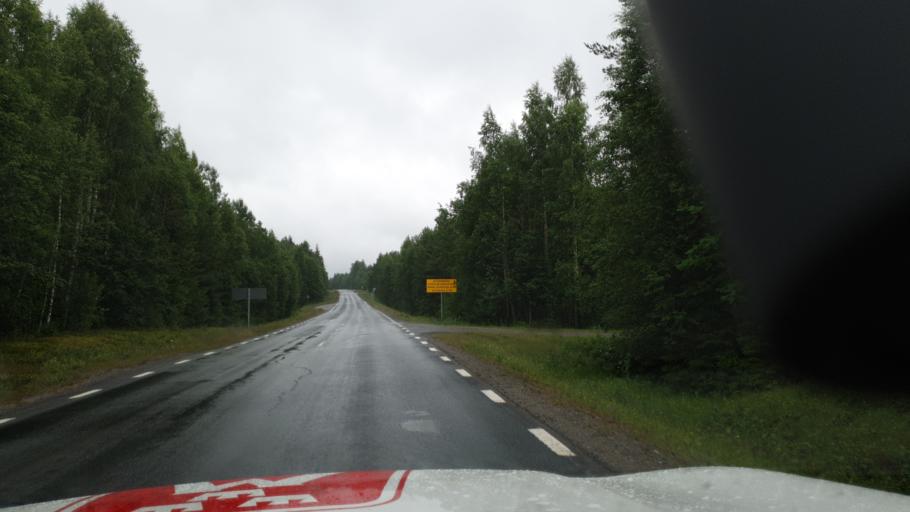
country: SE
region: Vaesterbotten
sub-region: Vannas Kommun
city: Vaennaes
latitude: 63.7717
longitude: 19.6962
